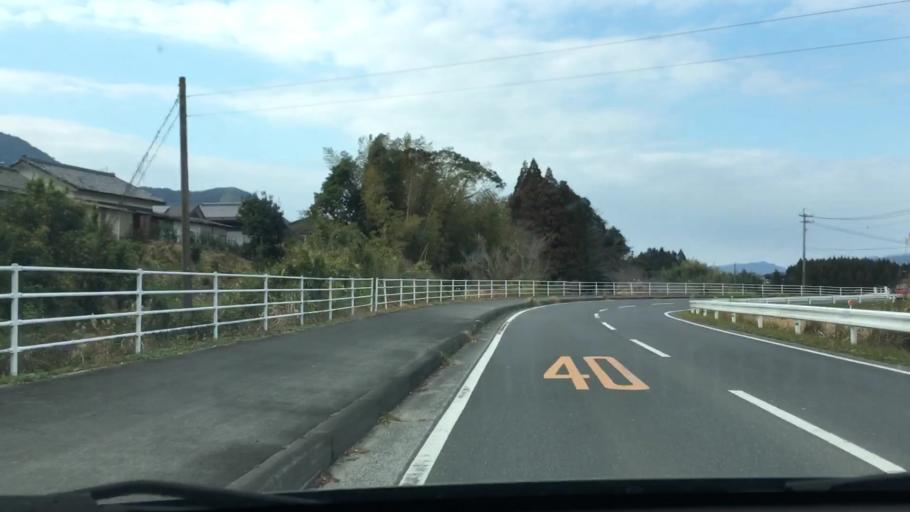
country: JP
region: Miyazaki
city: Kushima
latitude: 31.4984
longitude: 131.2386
